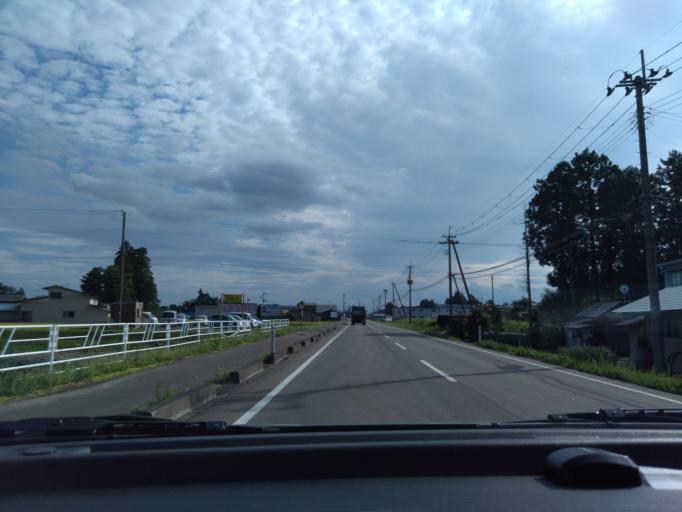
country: JP
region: Iwate
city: Hanamaki
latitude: 39.4546
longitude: 141.0989
